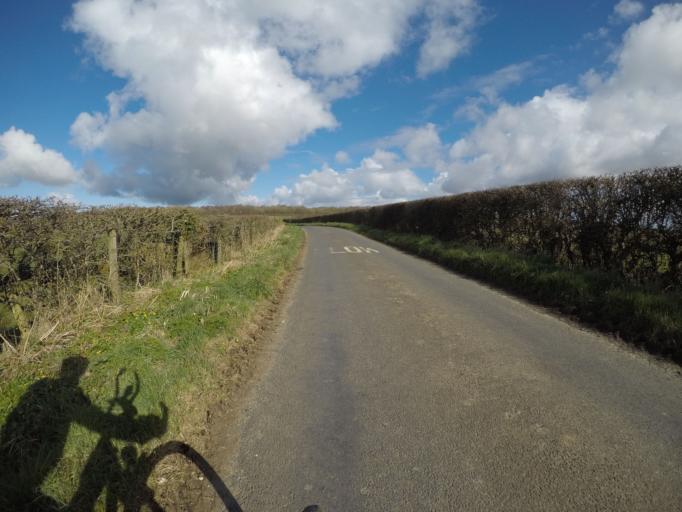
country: GB
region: Scotland
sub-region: North Ayrshire
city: Irvine
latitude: 55.6684
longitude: -4.6510
